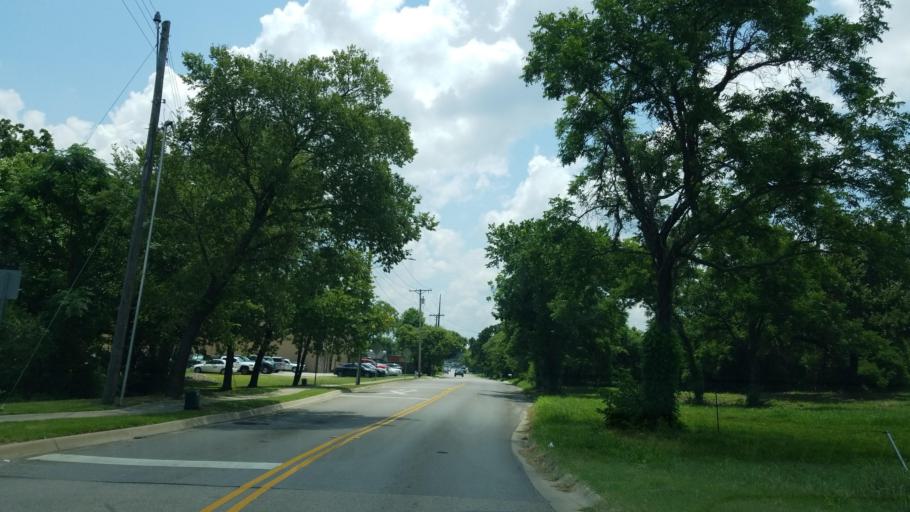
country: US
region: Texas
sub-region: Denton County
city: Denton
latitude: 33.2043
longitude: -97.1229
